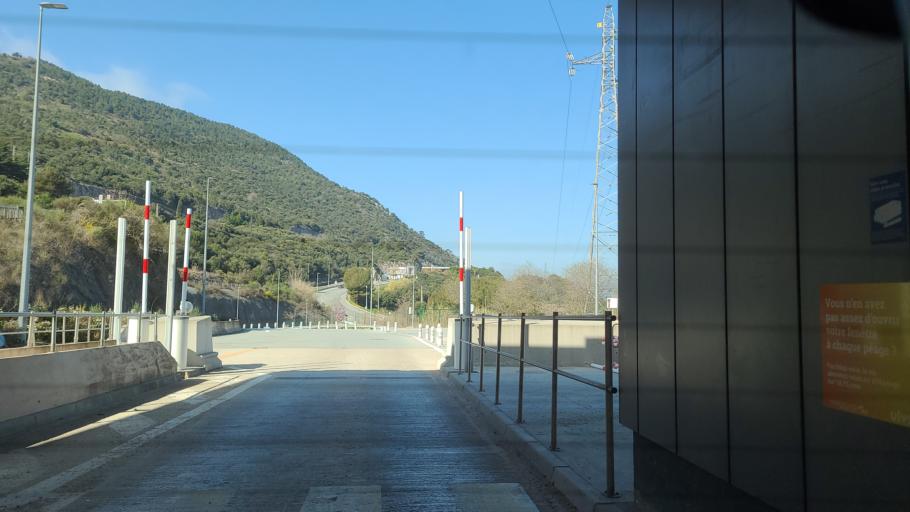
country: FR
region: Provence-Alpes-Cote d'Azur
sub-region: Departement des Alpes-Maritimes
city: La Turbie
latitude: 43.7454
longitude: 7.3785
